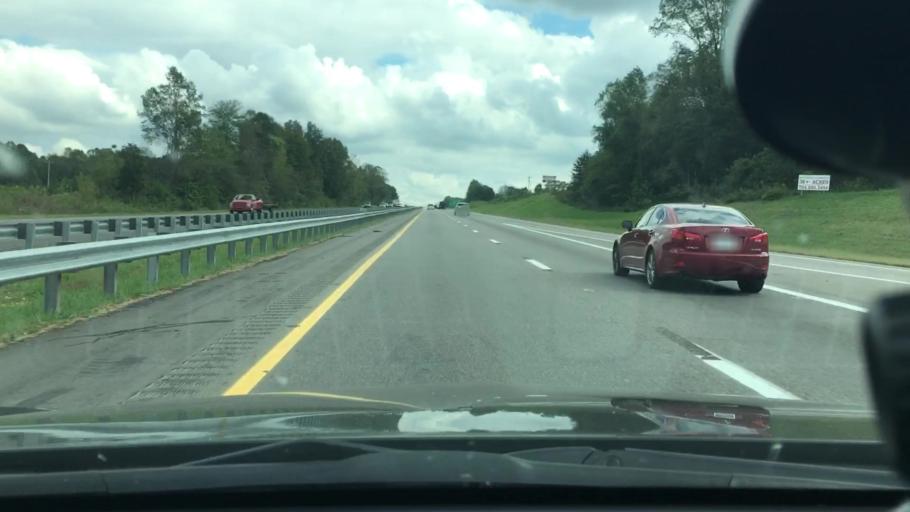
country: US
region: North Carolina
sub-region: Iredell County
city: Statesville
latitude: 35.8110
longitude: -80.8531
